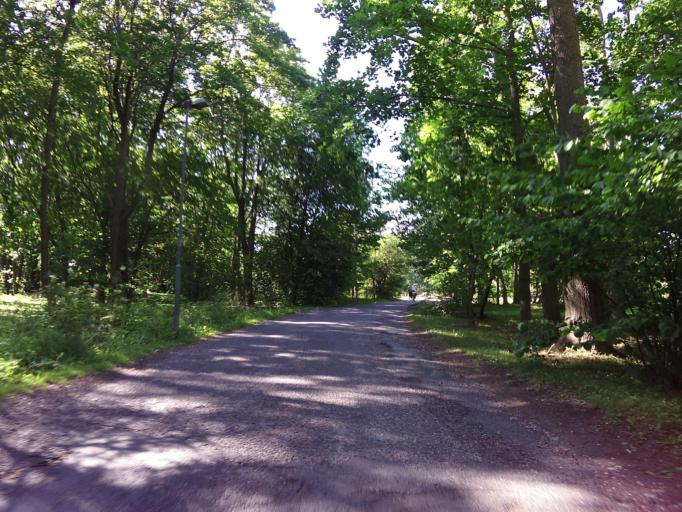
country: EE
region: Hiiumaa
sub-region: Kaerdla linn
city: Kardla
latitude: 59.0042
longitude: 22.7447
